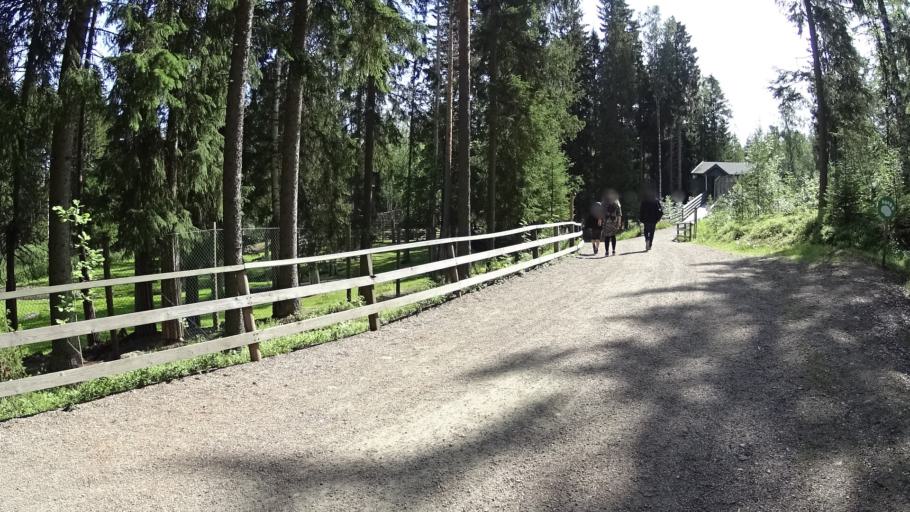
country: FI
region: Southern Ostrobothnia
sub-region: Kuusiokunnat
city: AEhtaeri
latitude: 62.5383
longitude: 24.1862
